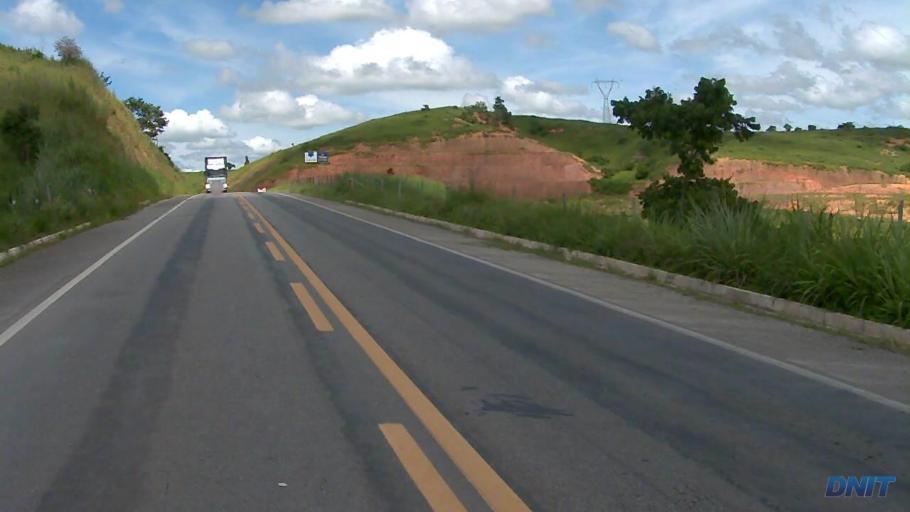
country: BR
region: Minas Gerais
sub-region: Governador Valadares
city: Governador Valadares
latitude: -19.0314
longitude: -42.1488
